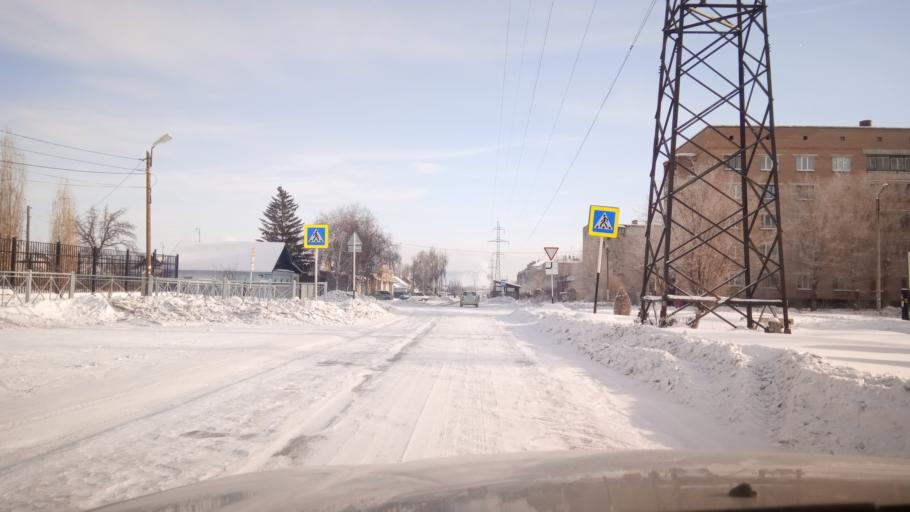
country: RU
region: Orenburg
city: Novotroitsk
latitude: 51.2115
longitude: 58.2955
